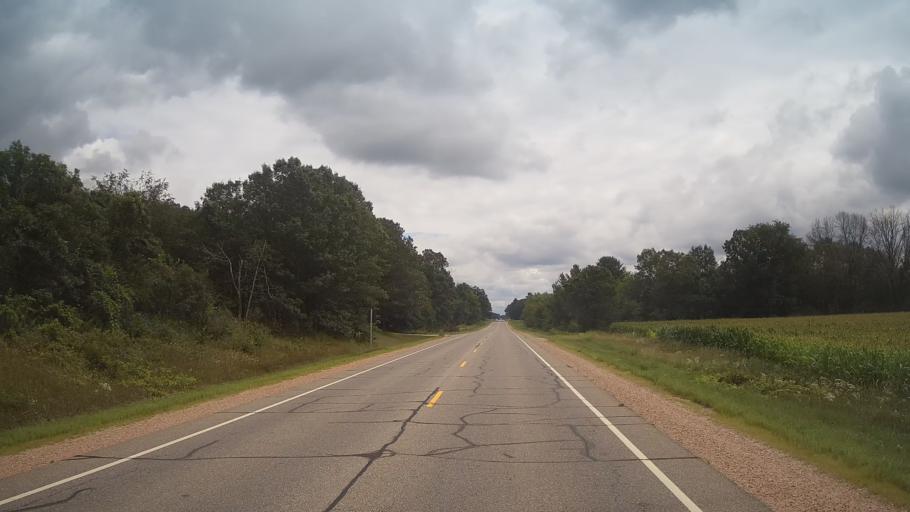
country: US
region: Wisconsin
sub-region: Adams County
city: Friendship
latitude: 44.0393
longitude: -89.9346
